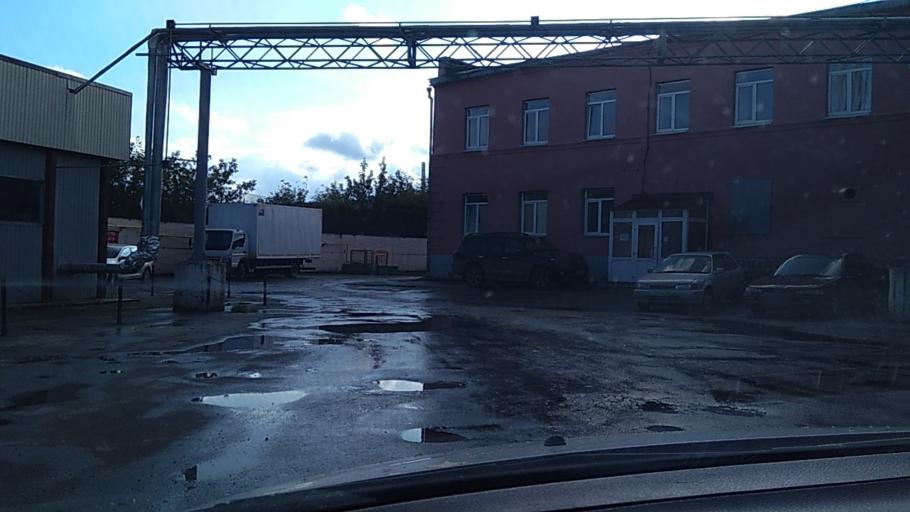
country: RU
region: Sverdlovsk
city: Sovkhoznyy
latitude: 56.7730
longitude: 60.6183
